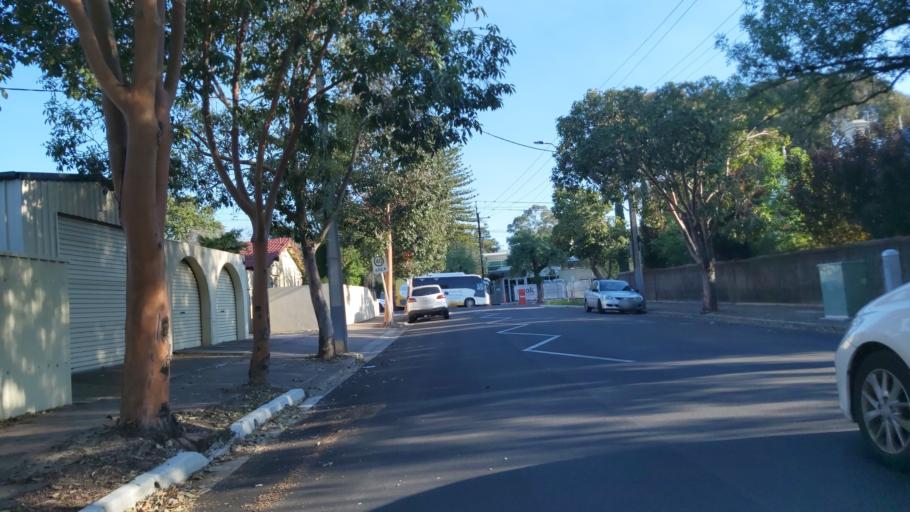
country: AU
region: South Australia
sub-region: Unley
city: Fullarton
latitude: -34.9535
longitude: 138.6218
